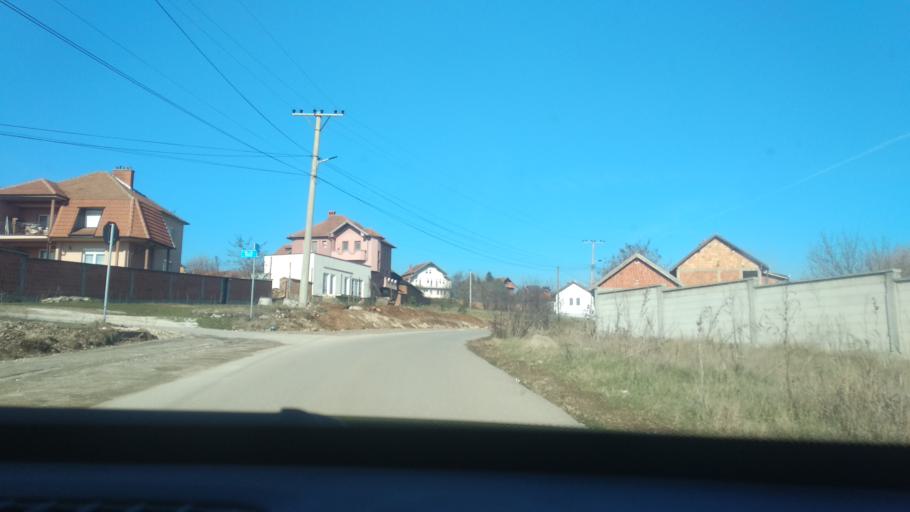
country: XK
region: Pristina
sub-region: Komuna e Gracanices
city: Glanica
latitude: 42.6040
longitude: 21.0282
